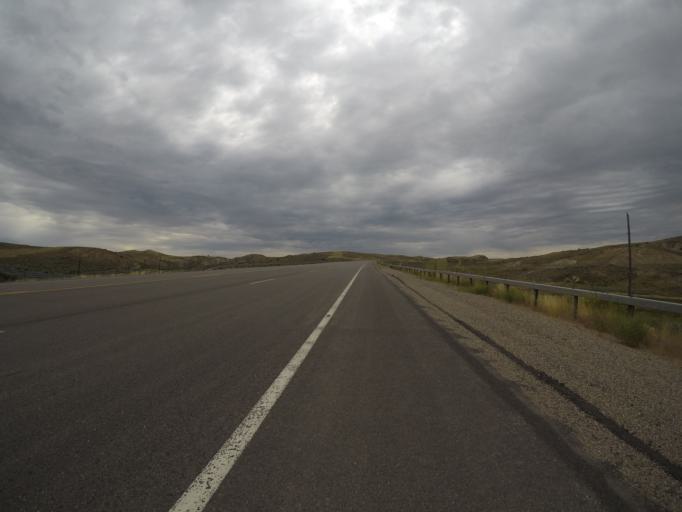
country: US
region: Wyoming
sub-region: Lincoln County
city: Kemmerer
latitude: 41.8092
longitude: -110.6147
